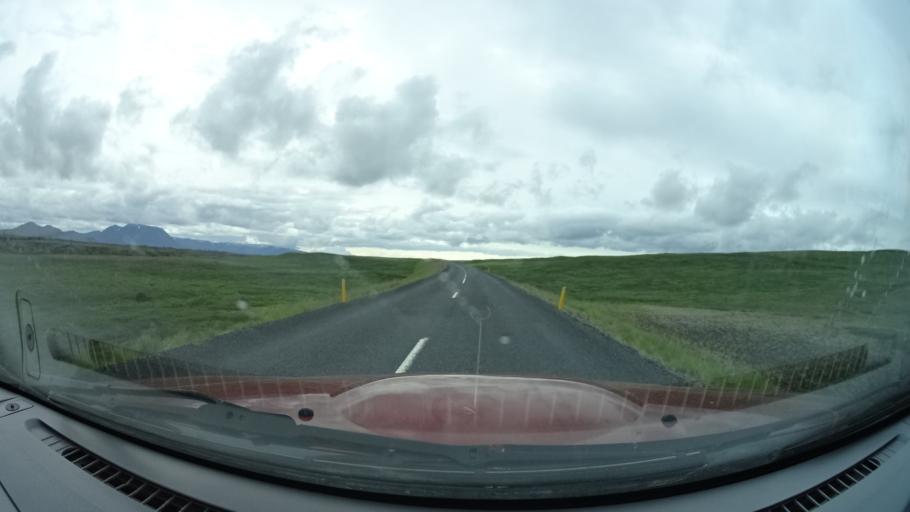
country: IS
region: Northeast
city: Laugar
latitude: 65.6533
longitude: -16.6068
